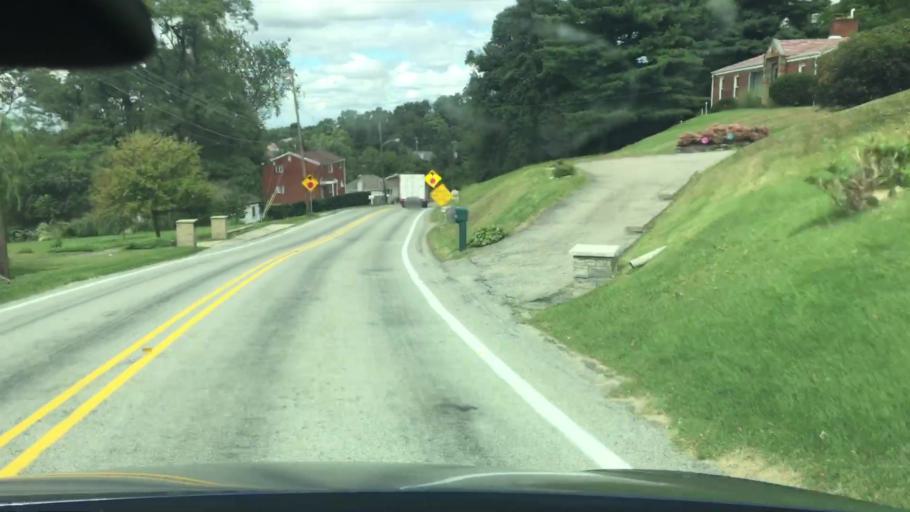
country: US
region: Pennsylvania
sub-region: Allegheny County
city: Penn Hills
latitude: 40.4860
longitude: -79.8207
